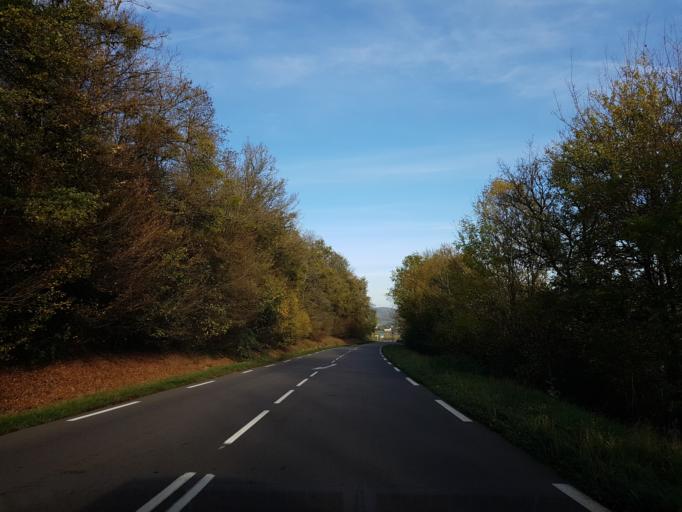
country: FR
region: Bourgogne
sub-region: Departement de la Cote-d'Or
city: Fleurey-sur-Ouche
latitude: 47.3073
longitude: 4.7207
